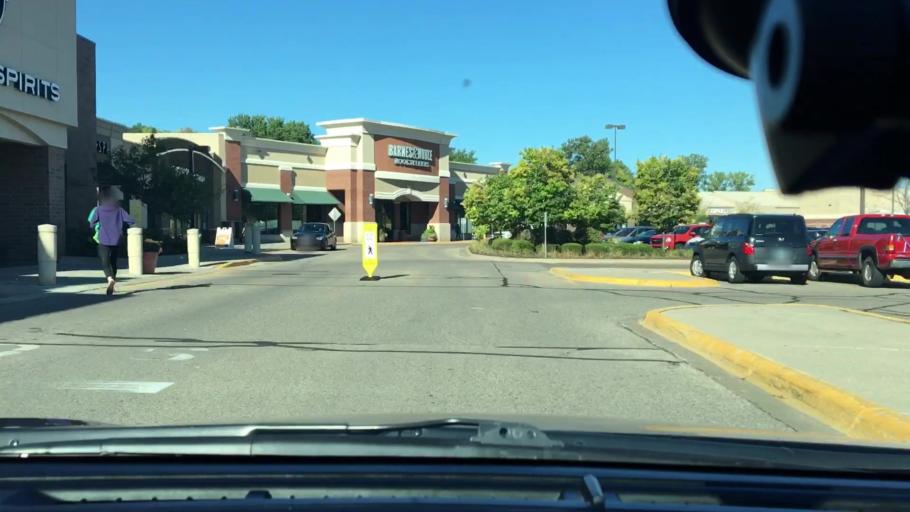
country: US
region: Minnesota
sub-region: Hennepin County
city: Minnetonka Mills
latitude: 44.9686
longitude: -93.4461
